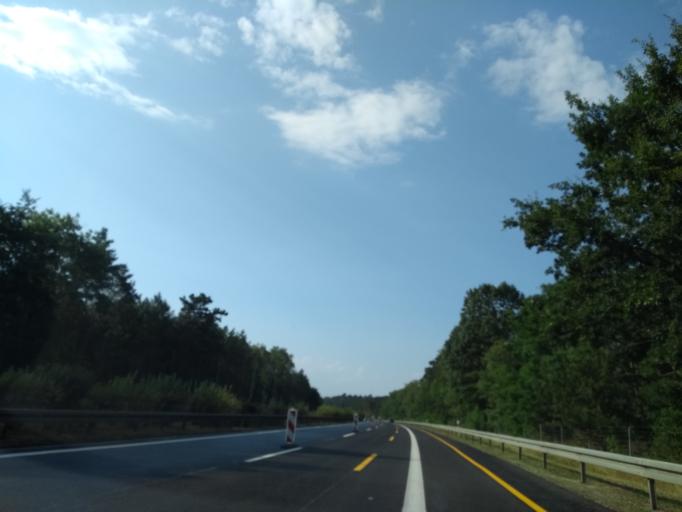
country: DE
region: Brandenburg
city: Bronkow
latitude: 51.6457
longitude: 13.9423
